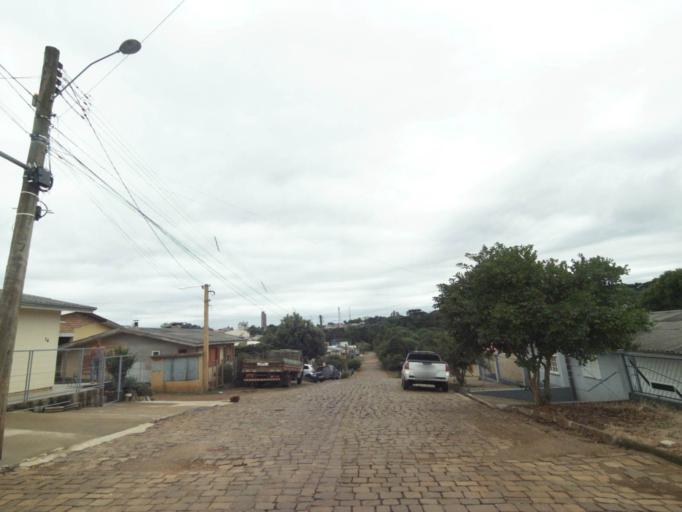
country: BR
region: Rio Grande do Sul
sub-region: Lagoa Vermelha
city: Lagoa Vermelha
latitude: -28.2177
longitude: -51.5309
